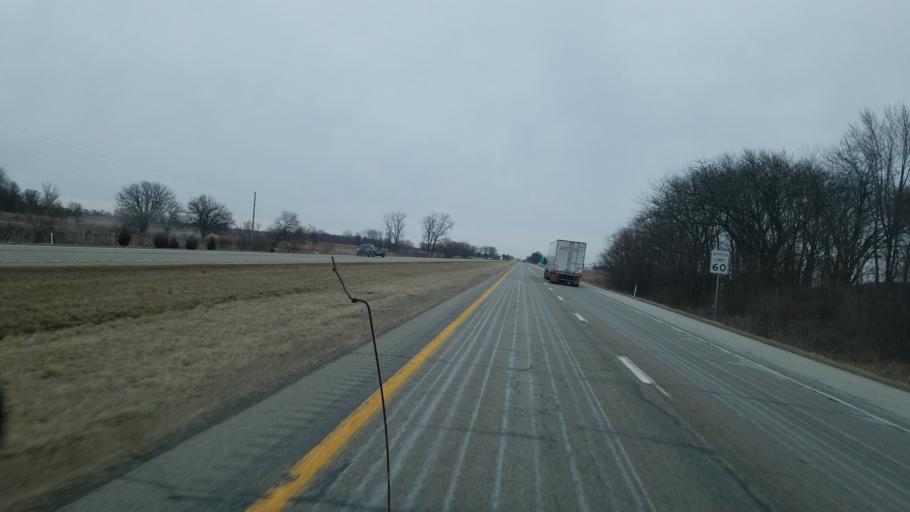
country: US
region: Indiana
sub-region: LaPorte County
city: Kingsford Heights
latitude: 41.3938
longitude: -86.6521
